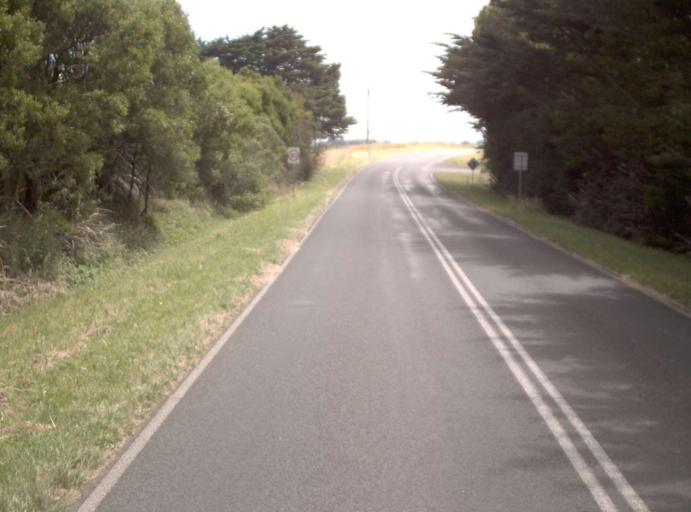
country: AU
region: Victoria
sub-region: Baw Baw
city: Warragul
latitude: -38.4115
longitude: 145.8100
